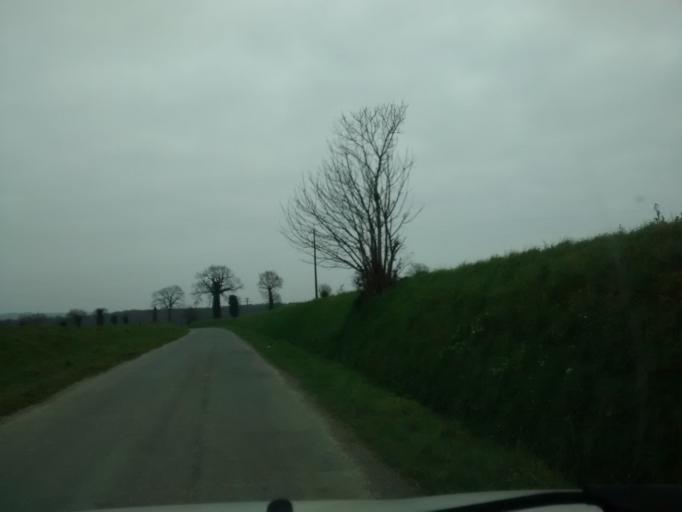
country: FR
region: Brittany
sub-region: Departement d'Ille-et-Vilaine
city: Bazouges-la-Perouse
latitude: 48.4058
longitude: -1.5514
